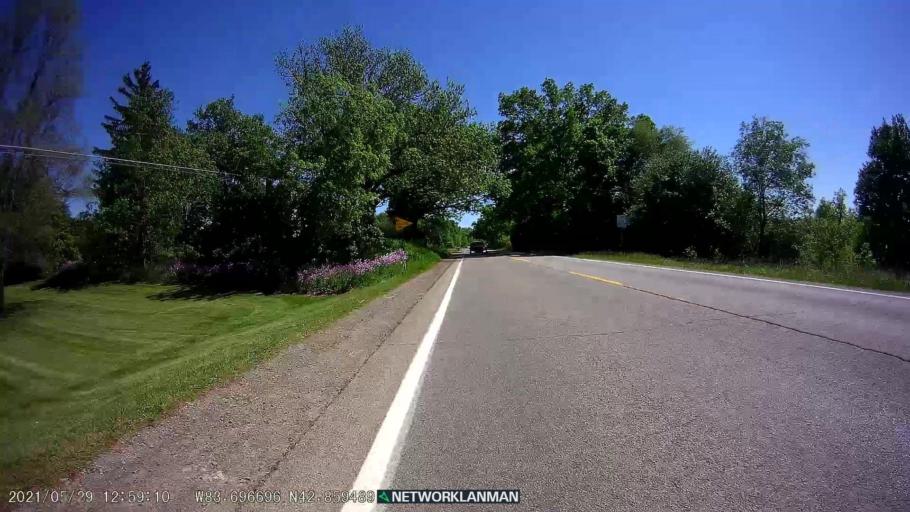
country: US
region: Michigan
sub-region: Genesee County
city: Lake Fenton
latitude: 42.8598
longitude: -83.6967
